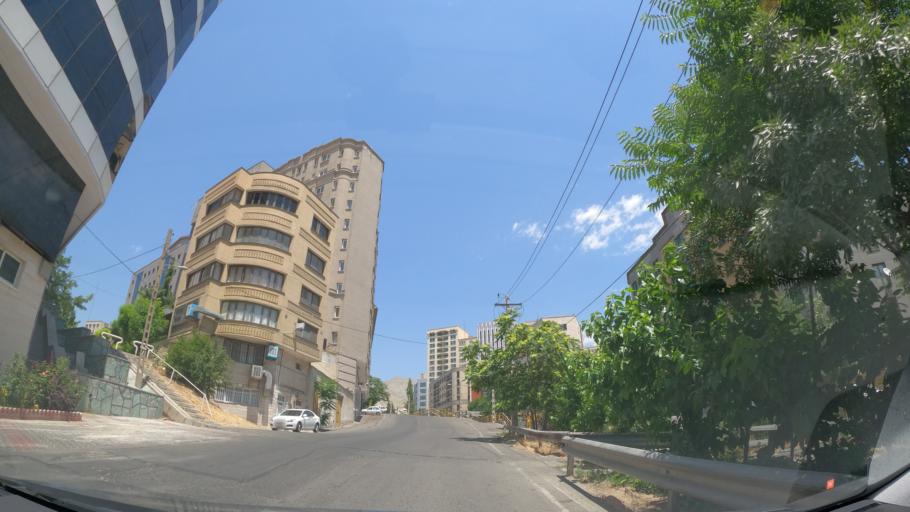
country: IR
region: Tehran
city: Tajrish
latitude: 35.7805
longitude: 51.3863
